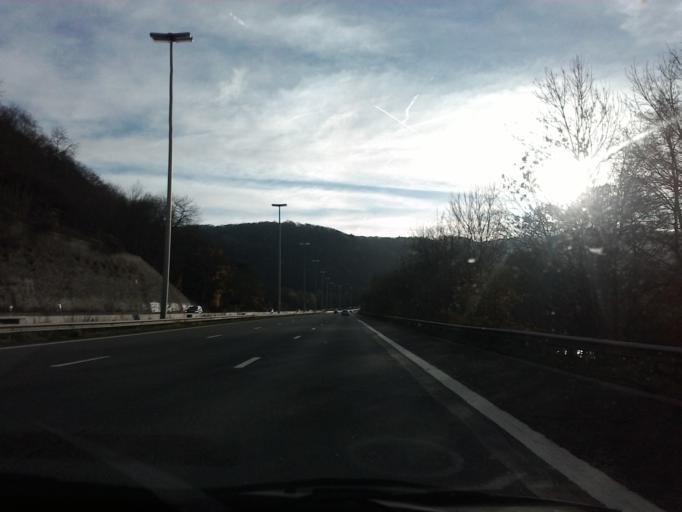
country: BE
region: Wallonia
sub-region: Province de Liege
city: Chaudfontaine
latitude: 50.5817
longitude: 5.5991
